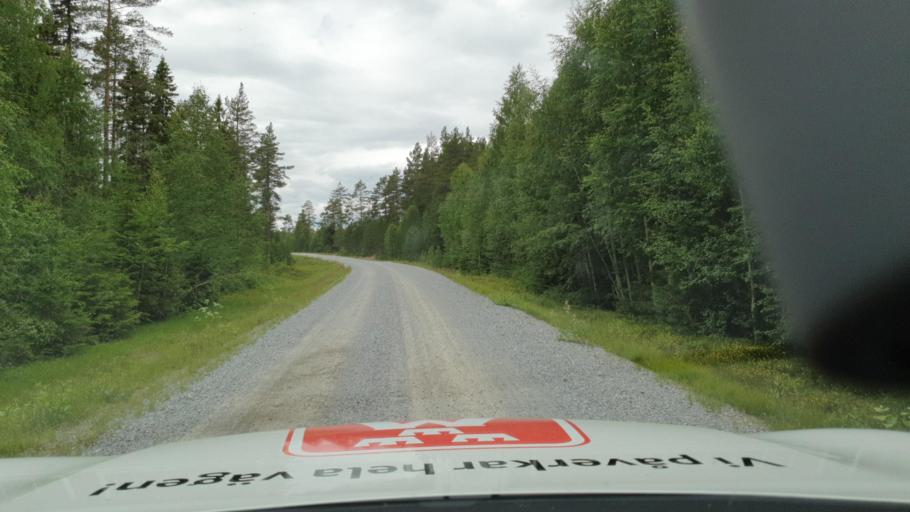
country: SE
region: Vaesterbotten
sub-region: Nordmalings Kommun
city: Nordmaling
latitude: 63.7378
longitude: 19.4110
